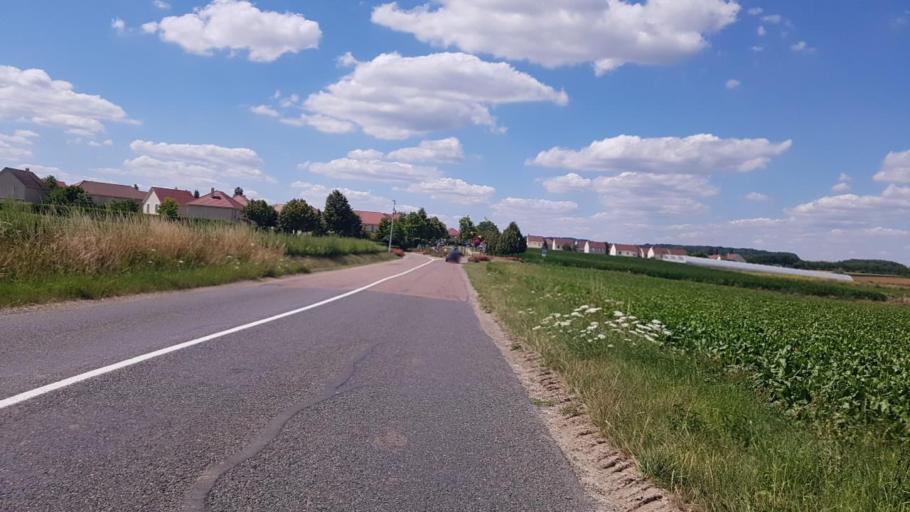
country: FR
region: Ile-de-France
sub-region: Departement de Seine-et-Marne
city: Moussy-le-Neuf
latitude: 49.0581
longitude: 2.6122
